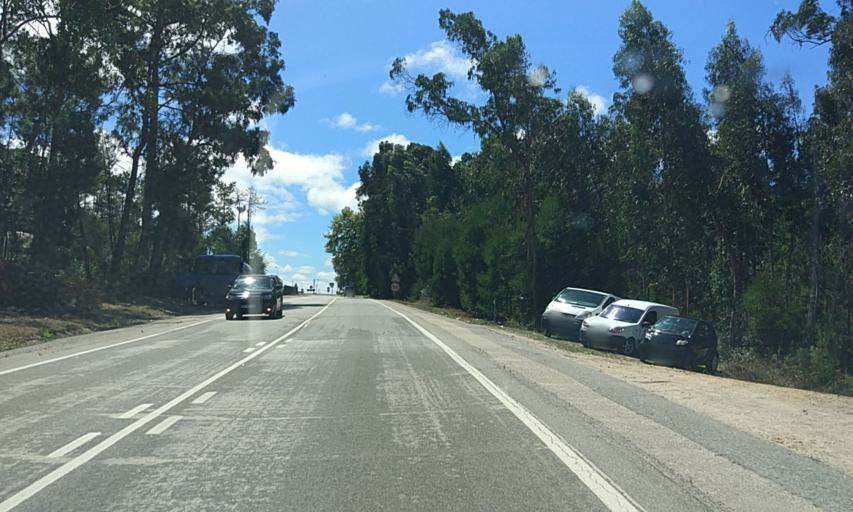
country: PT
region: Aveiro
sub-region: Vagos
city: Vagos
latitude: 40.5060
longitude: -8.6791
